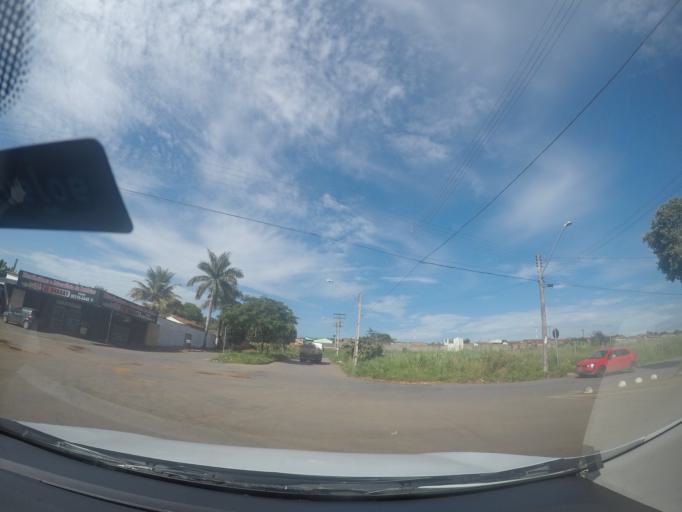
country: BR
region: Goias
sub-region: Goiania
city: Goiania
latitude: -16.6627
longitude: -49.2073
